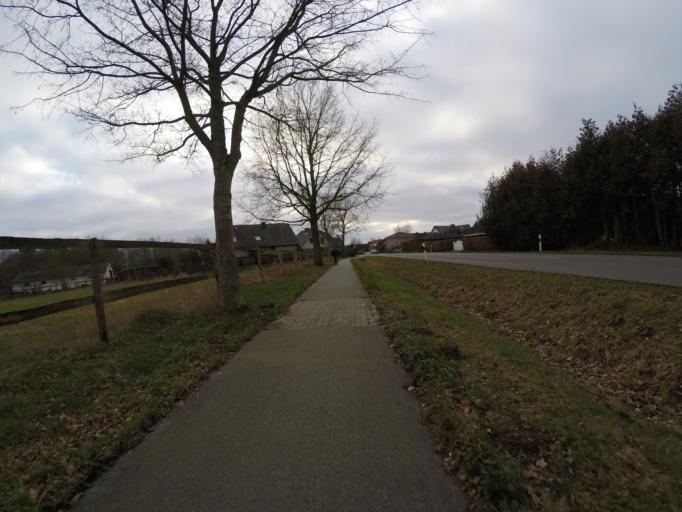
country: DE
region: Schleswig-Holstein
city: Alveslohe
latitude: 53.7950
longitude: 9.9189
